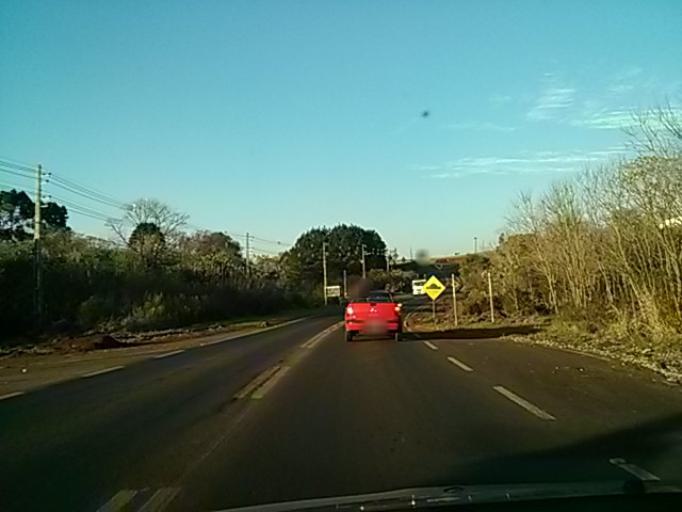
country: BR
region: Santa Catarina
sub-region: Chapeco
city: Chapeco
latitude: -27.1046
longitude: -52.7066
